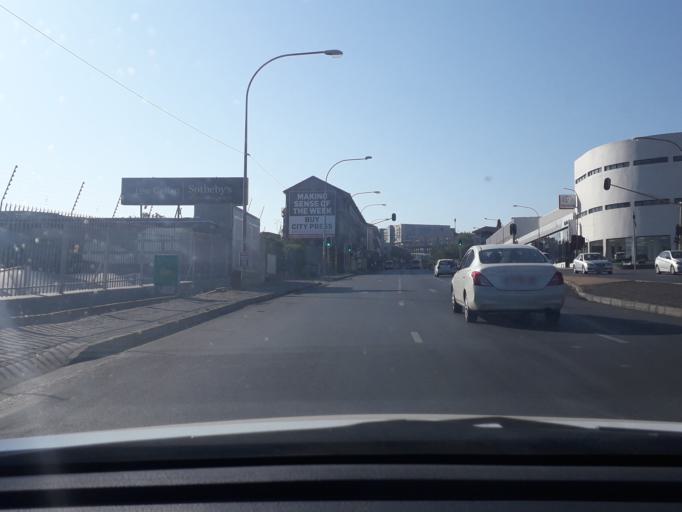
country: ZA
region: Gauteng
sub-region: City of Johannesburg Metropolitan Municipality
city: Johannesburg
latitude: -26.1191
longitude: 28.0270
